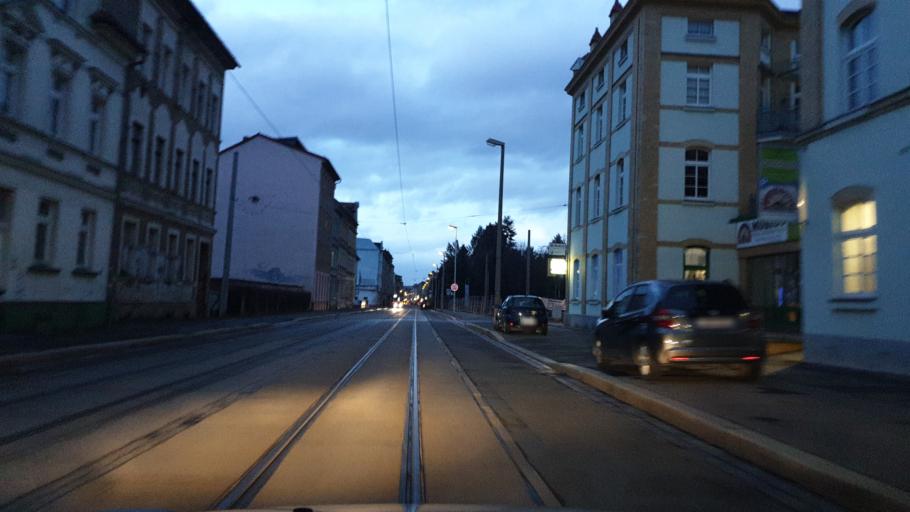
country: DE
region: Thuringia
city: Gera
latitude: 50.8595
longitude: 12.0729
